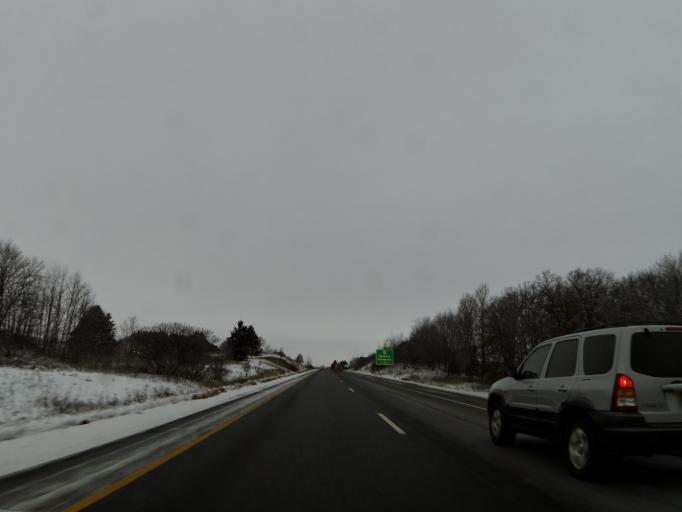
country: US
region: Wisconsin
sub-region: Saint Croix County
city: Baldwin
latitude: 44.9383
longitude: -92.3484
